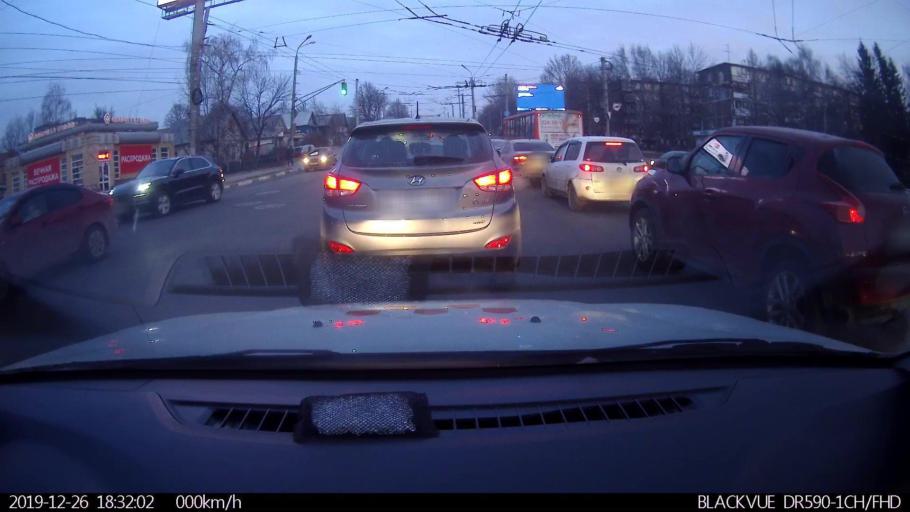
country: RU
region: Nizjnij Novgorod
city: Nizhniy Novgorod
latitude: 56.2968
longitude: 44.0336
